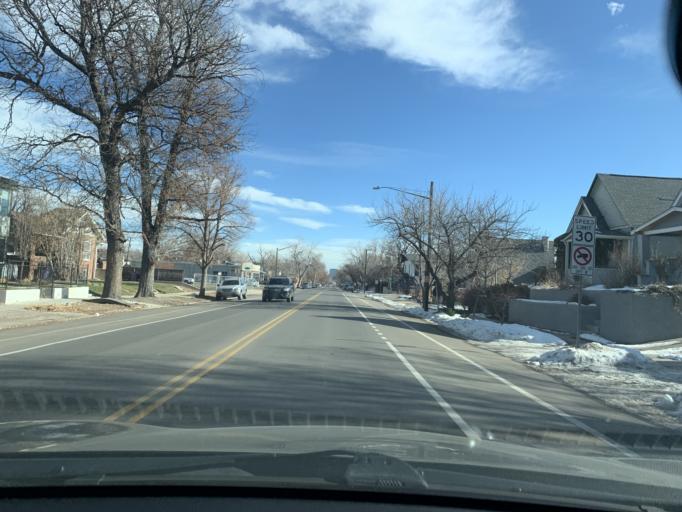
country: US
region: Colorado
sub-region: Jefferson County
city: Edgewater
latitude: 39.7512
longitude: -105.0342
